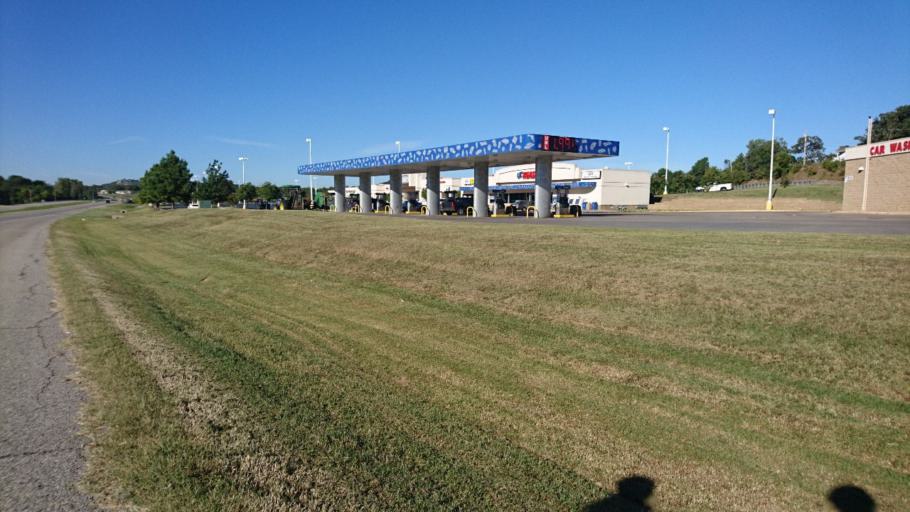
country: US
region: Oklahoma
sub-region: Rogers County
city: Catoosa
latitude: 36.1910
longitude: -95.7350
